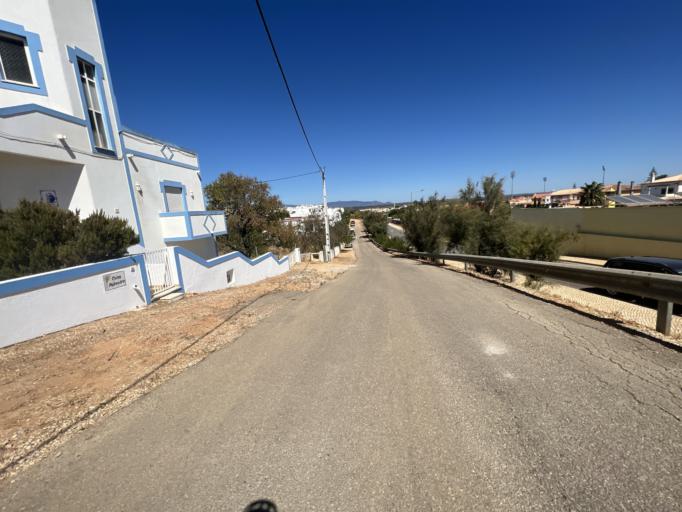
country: PT
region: Faro
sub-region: Portimao
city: Portimao
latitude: 37.1299
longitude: -8.5108
